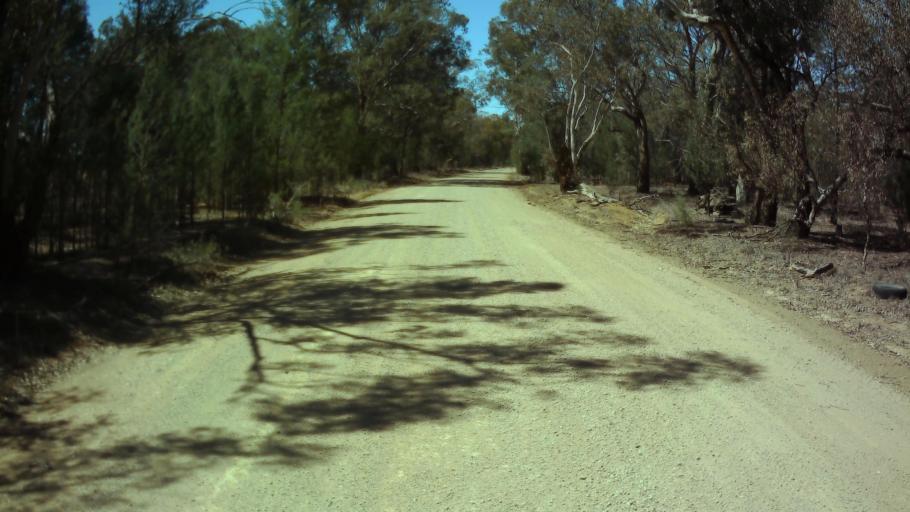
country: AU
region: New South Wales
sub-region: Weddin
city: Grenfell
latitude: -33.8612
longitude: 148.0873
